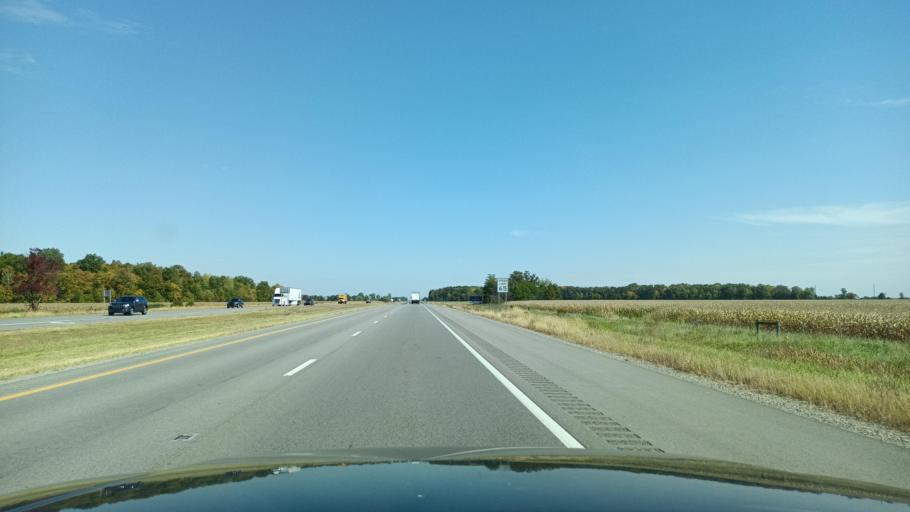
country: US
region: Ohio
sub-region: Defiance County
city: Defiance
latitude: 41.3324
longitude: -84.2840
